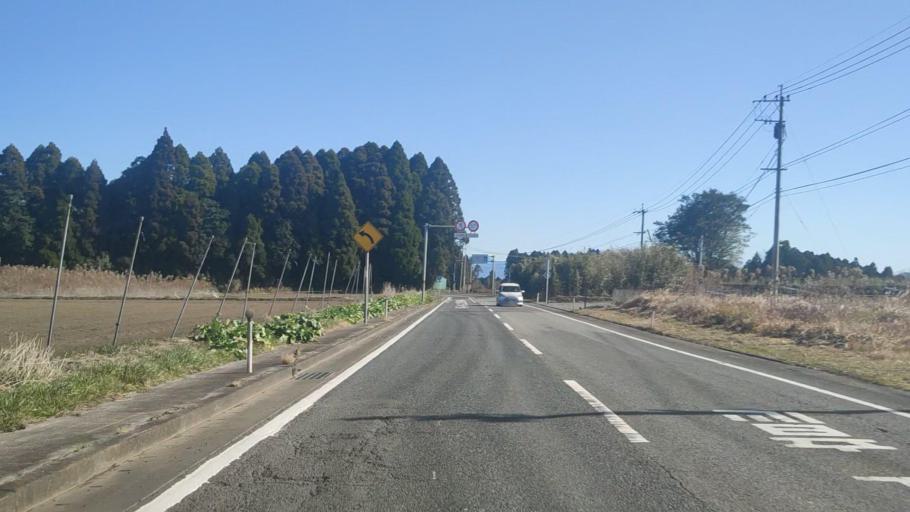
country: JP
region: Kagoshima
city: Sueyoshicho-ninokata
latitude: 31.6872
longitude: 130.9669
